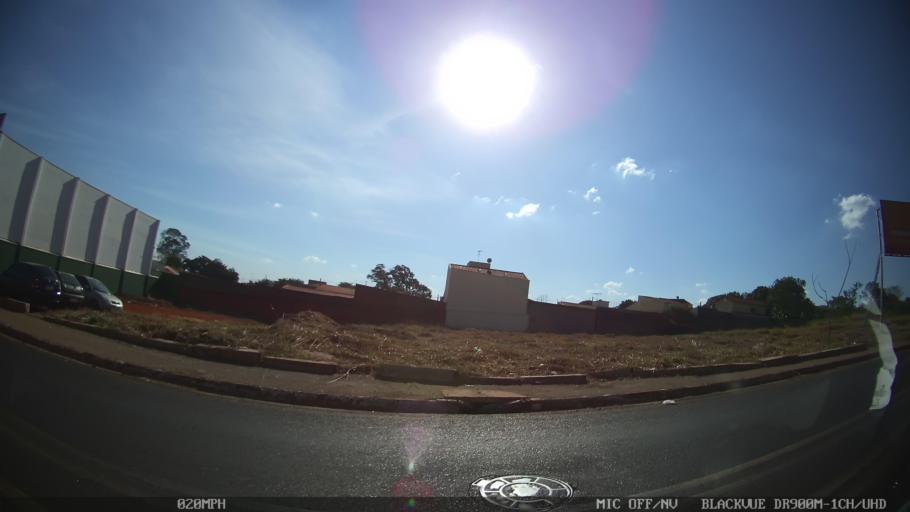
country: BR
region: Sao Paulo
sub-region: Ribeirao Preto
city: Ribeirao Preto
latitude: -21.1730
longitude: -47.7816
